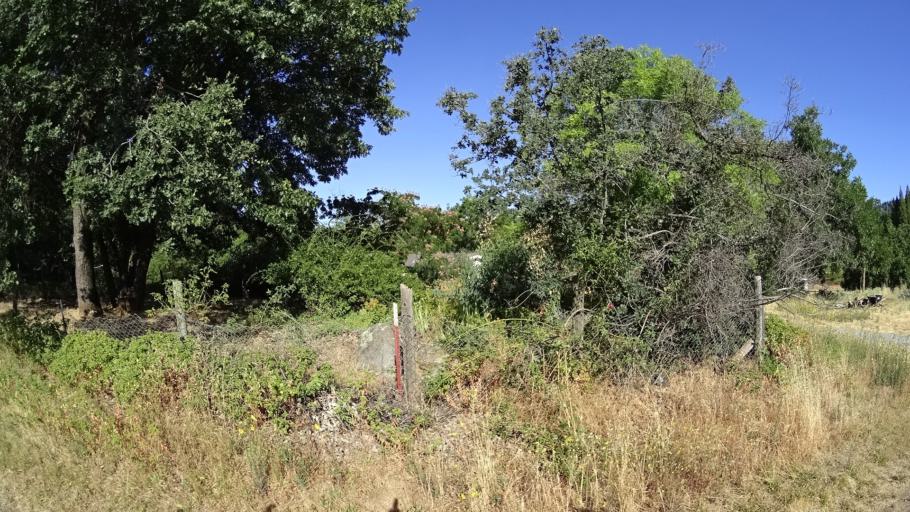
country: US
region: California
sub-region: Amador County
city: Pioneer
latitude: 38.4111
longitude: -120.5504
